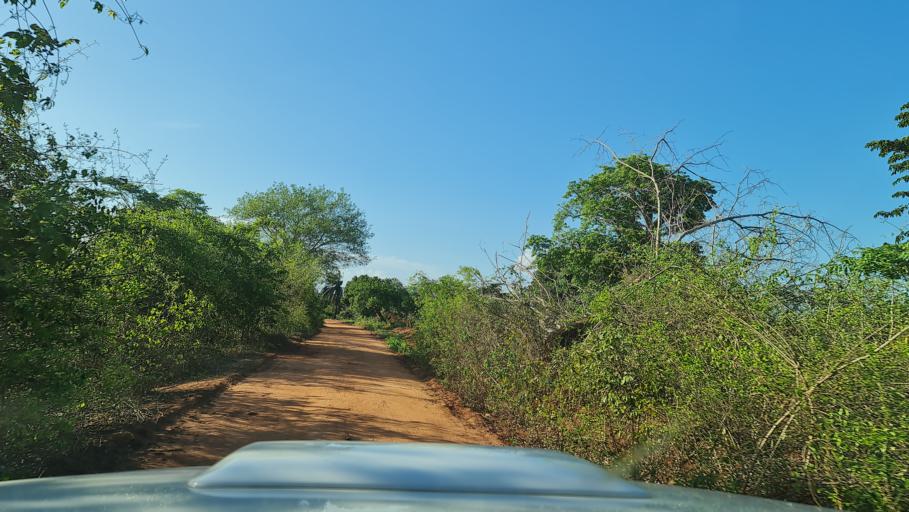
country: MZ
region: Nampula
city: Nacala
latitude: -14.7050
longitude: 40.3321
